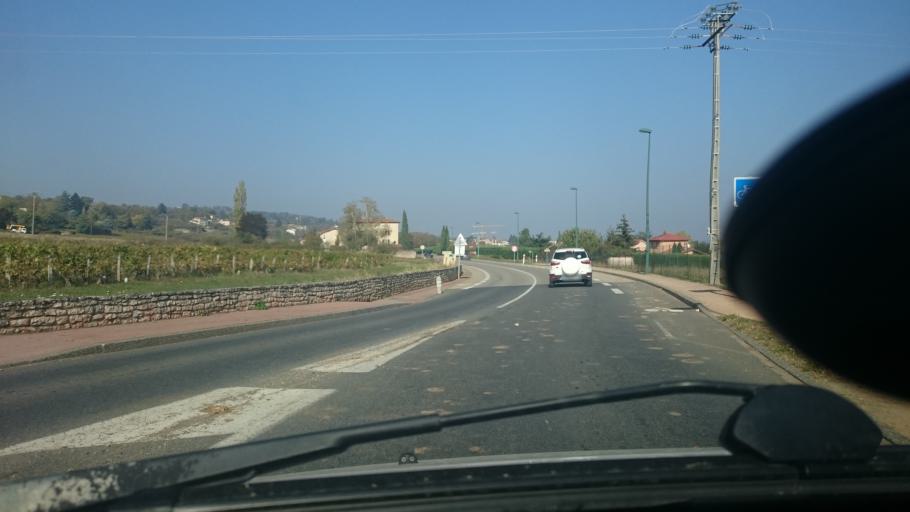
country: FR
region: Rhone-Alpes
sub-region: Departement du Rhone
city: Lucenay
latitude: 45.9174
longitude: 4.7059
